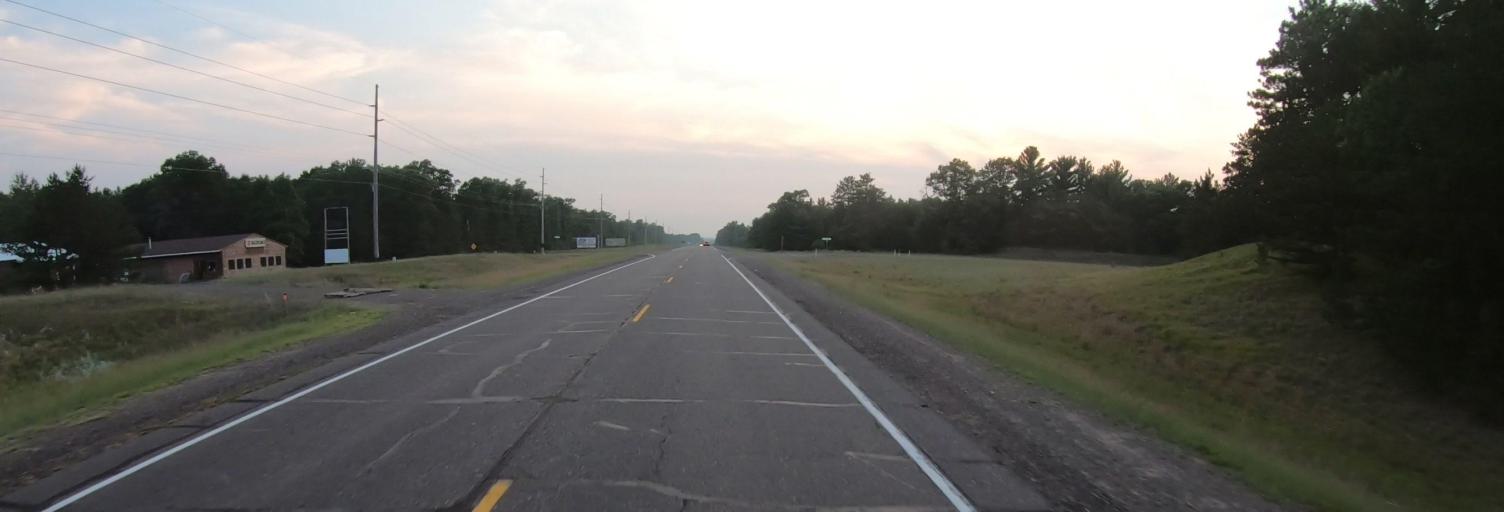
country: US
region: Wisconsin
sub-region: Burnett County
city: Grantsburg
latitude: 45.7731
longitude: -92.7426
